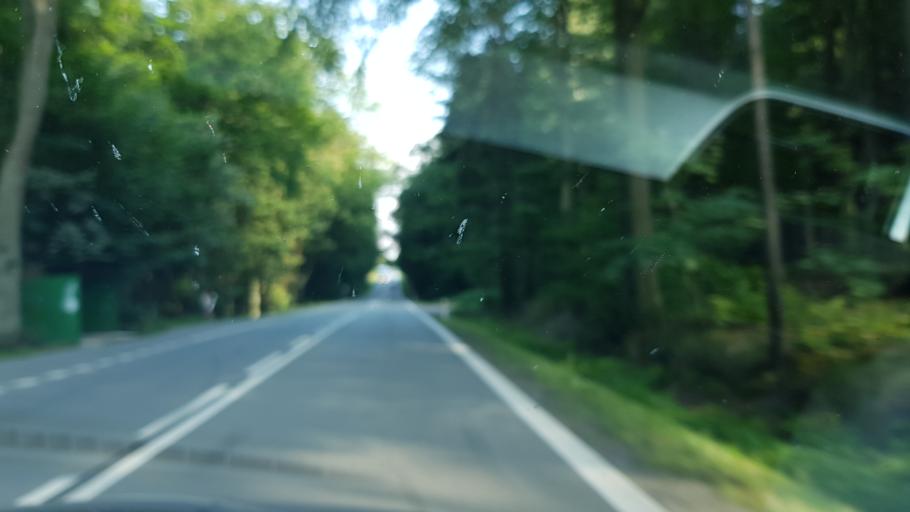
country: CZ
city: Vamberk
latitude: 50.1173
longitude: 16.3530
